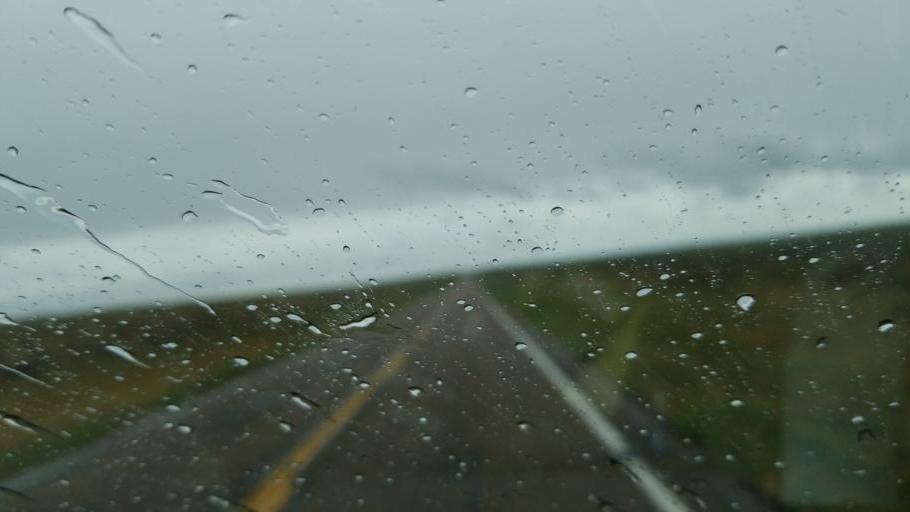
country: US
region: Colorado
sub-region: Lincoln County
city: Hugo
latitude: 38.8494
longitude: -103.2616
